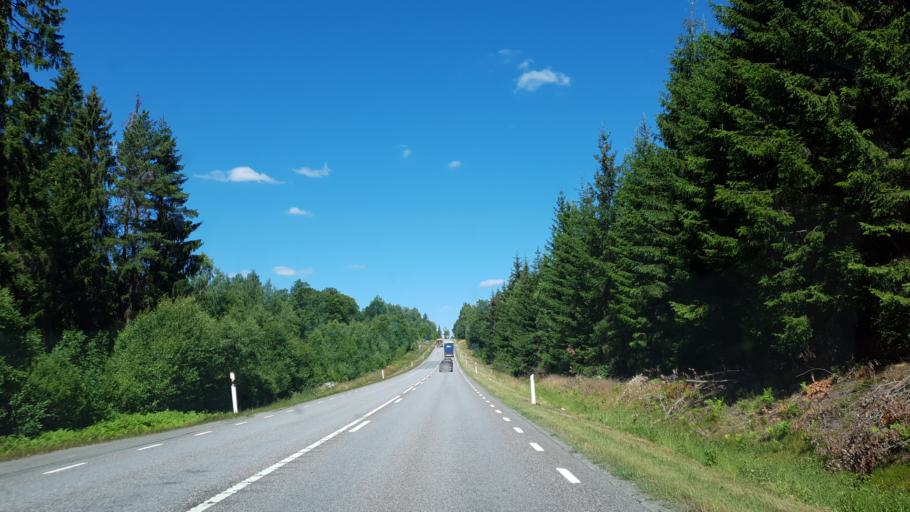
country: SE
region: Joenkoeping
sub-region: Varnamo Kommun
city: Rydaholm
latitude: 56.9430
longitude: 14.3633
